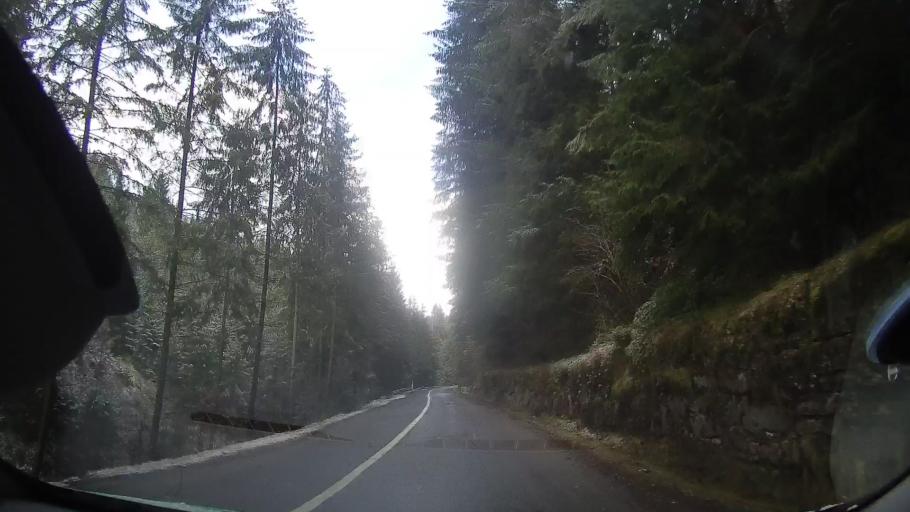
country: RO
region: Alba
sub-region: Comuna Horea
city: Horea
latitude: 46.4890
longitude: 22.9618
